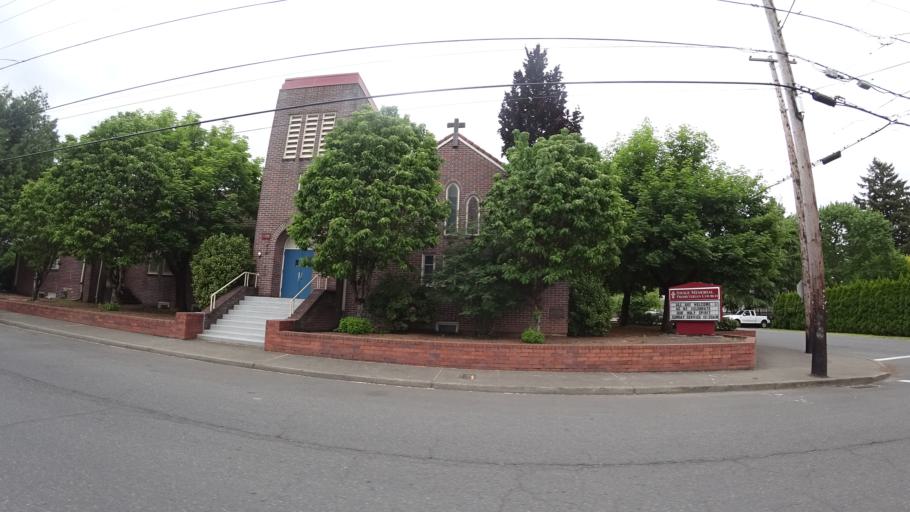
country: US
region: Oregon
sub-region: Multnomah County
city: Lents
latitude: 45.5104
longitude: -122.5210
